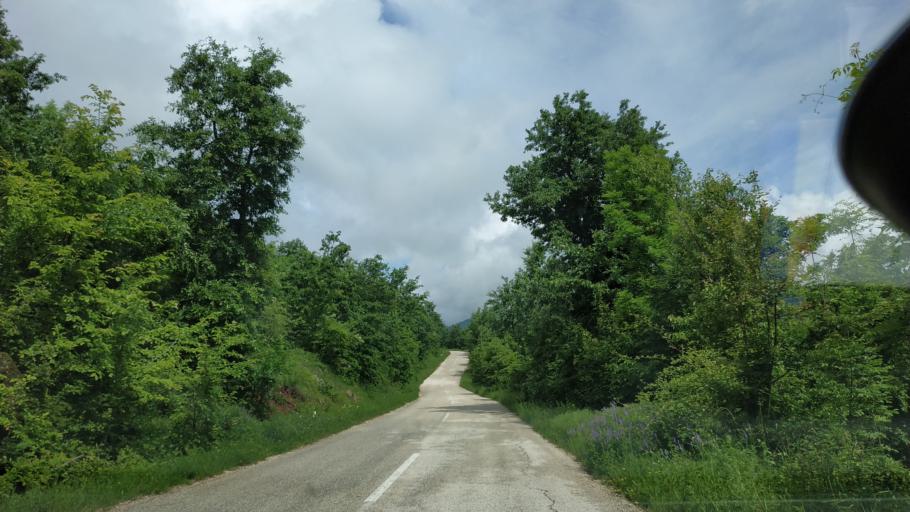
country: RS
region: Central Serbia
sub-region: Zajecarski Okrug
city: Boljevac
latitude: 43.7340
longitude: 21.9530
